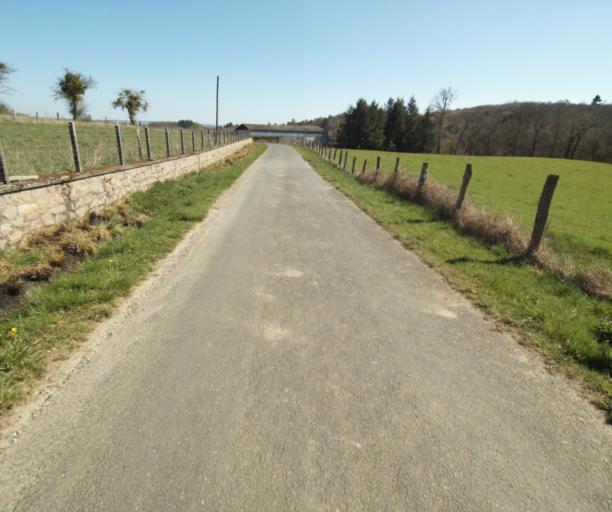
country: FR
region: Limousin
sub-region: Departement de la Correze
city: Saint-Mexant
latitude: 45.2851
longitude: 1.6997
